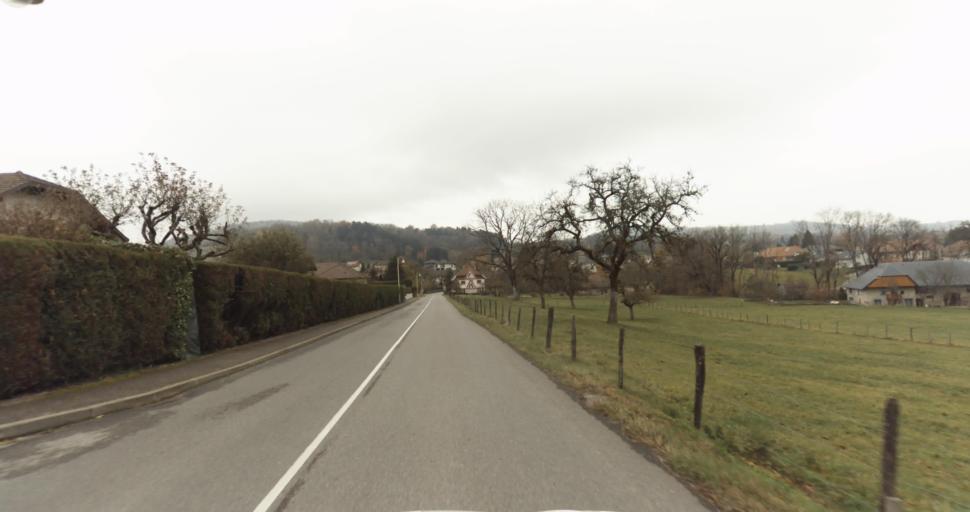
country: FR
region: Rhone-Alpes
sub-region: Departement de la Haute-Savoie
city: Cusy
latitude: 45.7697
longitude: 6.0269
